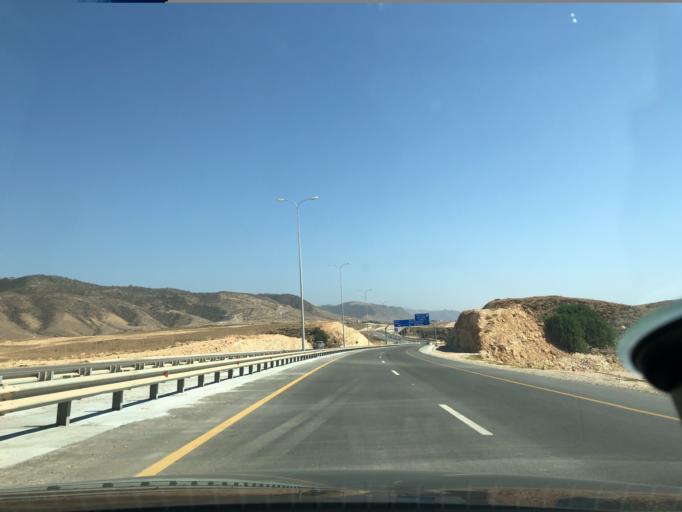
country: OM
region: Zufar
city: Salalah
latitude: 17.0585
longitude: 54.4200
